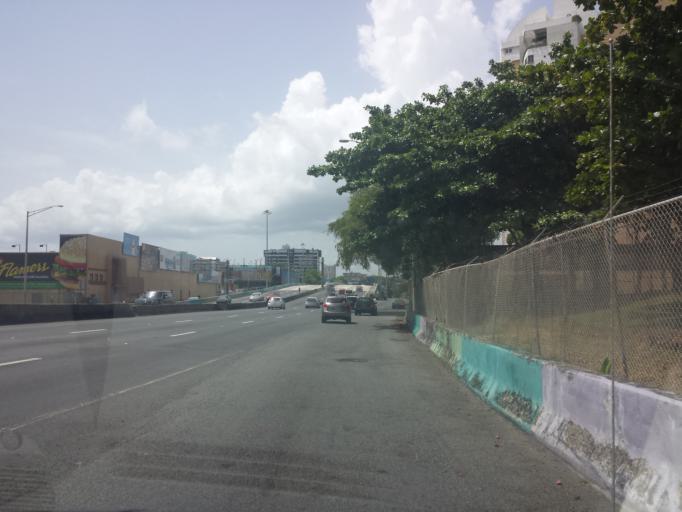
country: PR
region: Catano
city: Catano
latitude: 18.4062
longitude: -66.1078
